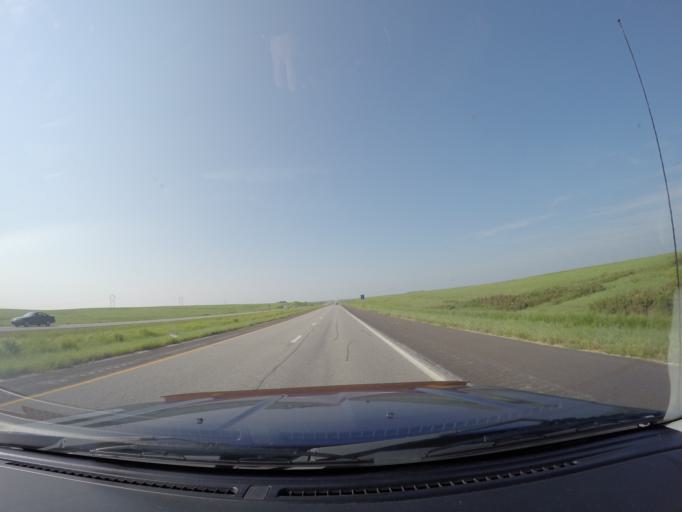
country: US
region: Kansas
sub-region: Riley County
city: Manhattan
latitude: 39.1171
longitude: -96.5384
